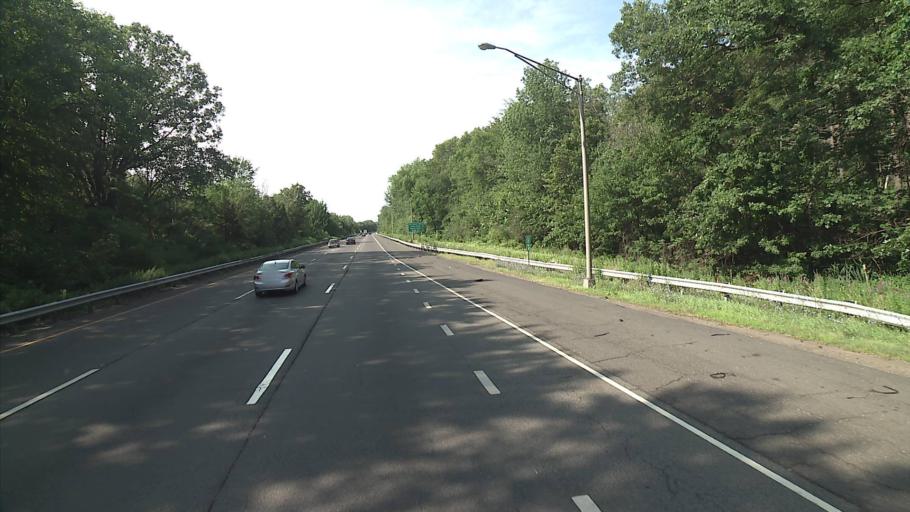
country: US
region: Connecticut
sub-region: Middlesex County
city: Cromwell
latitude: 41.6188
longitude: -72.6963
